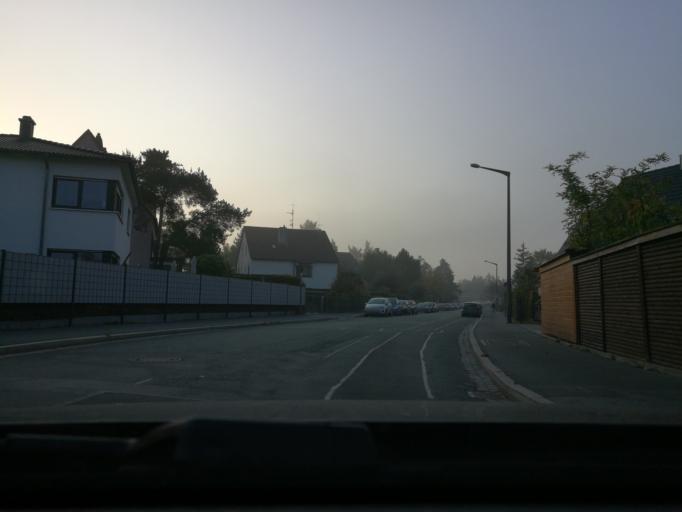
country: DE
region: Bavaria
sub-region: Regierungsbezirk Mittelfranken
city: Furth
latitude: 49.4852
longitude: 10.9652
